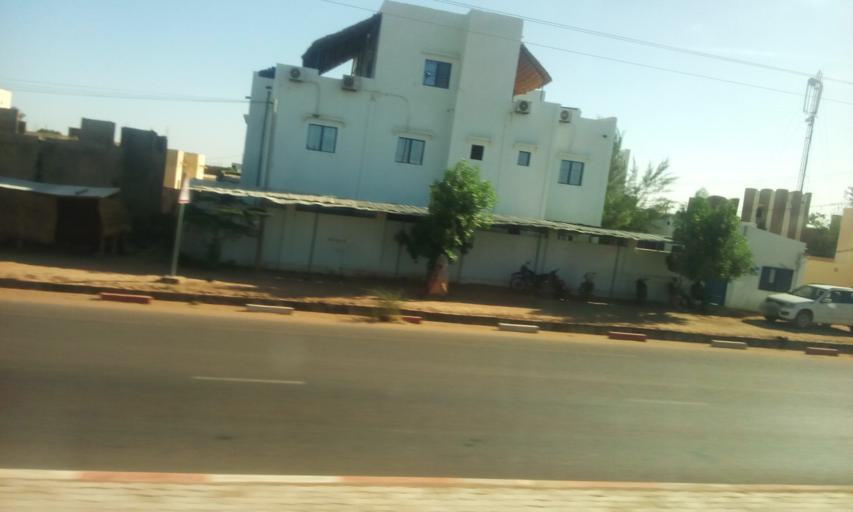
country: ML
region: Segou
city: Segou
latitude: 13.4212
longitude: -6.2957
